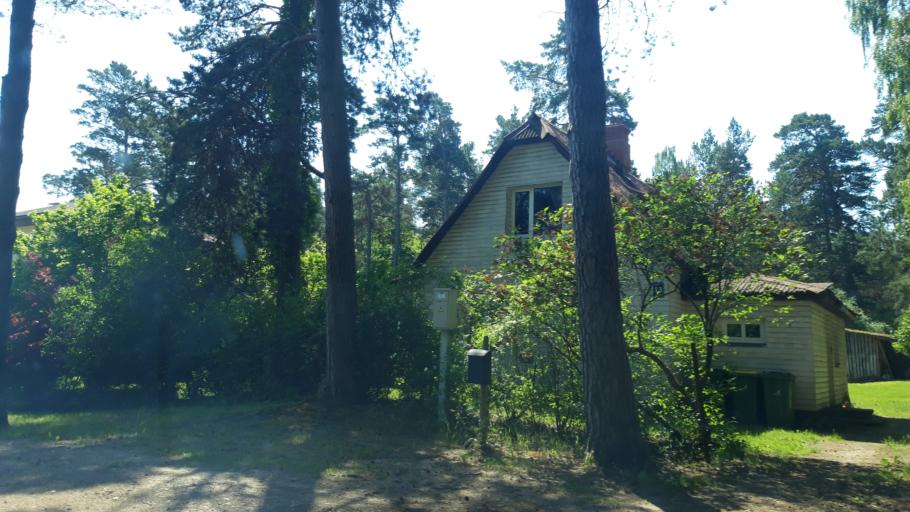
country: LV
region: Saulkrastu
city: Saulkrasti
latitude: 57.2574
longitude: 24.4099
